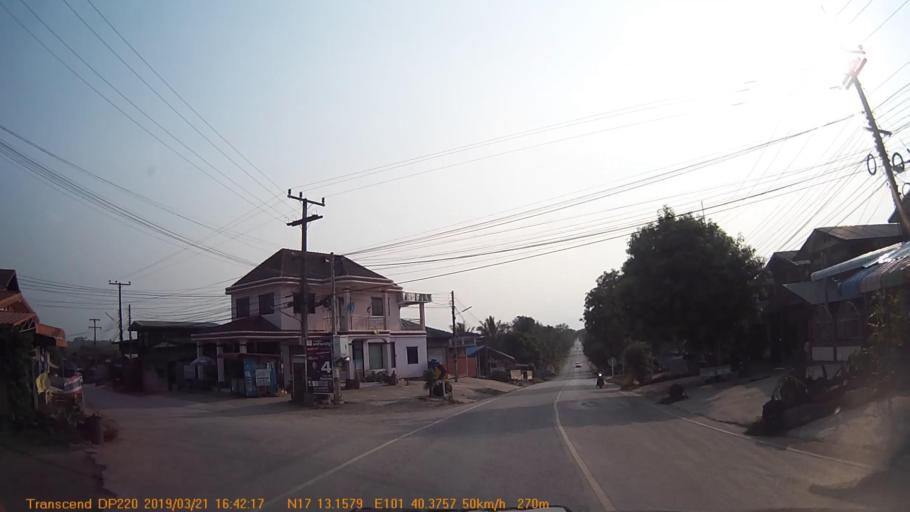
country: TH
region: Loei
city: Phu Luang
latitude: 17.2189
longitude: 101.6728
